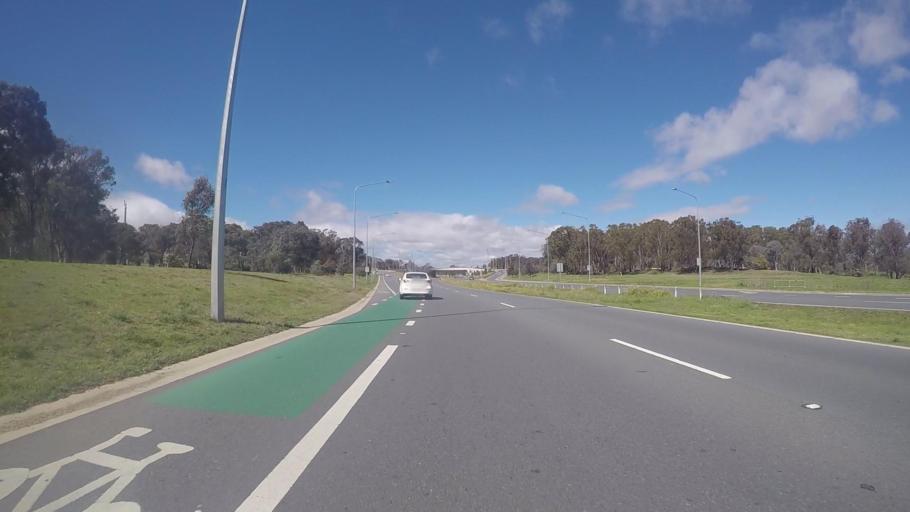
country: AU
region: Australian Capital Territory
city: Canberra
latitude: -35.2961
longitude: 149.1462
